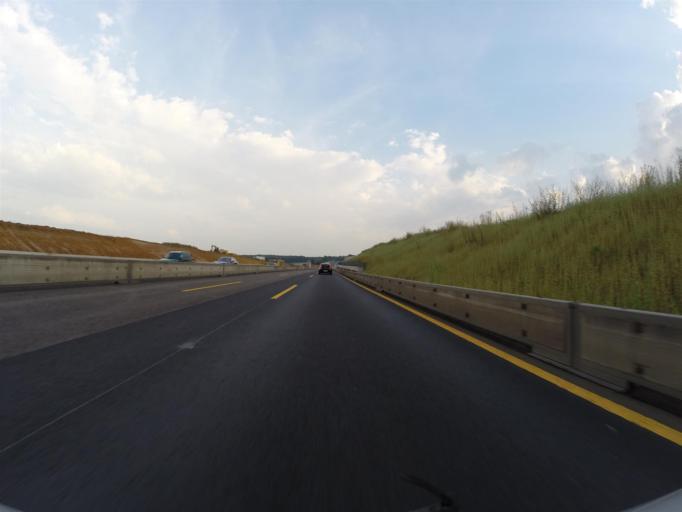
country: DE
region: Hesse
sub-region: Regierungsbezirk Kassel
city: Korle
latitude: 51.1402
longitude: 9.4752
